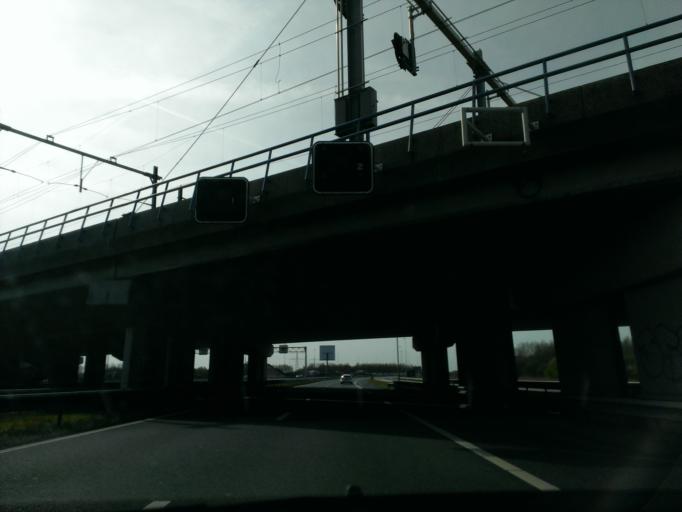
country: NL
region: North Holland
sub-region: Gemeente Amsterdam
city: Driemond
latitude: 52.3296
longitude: 5.0053
